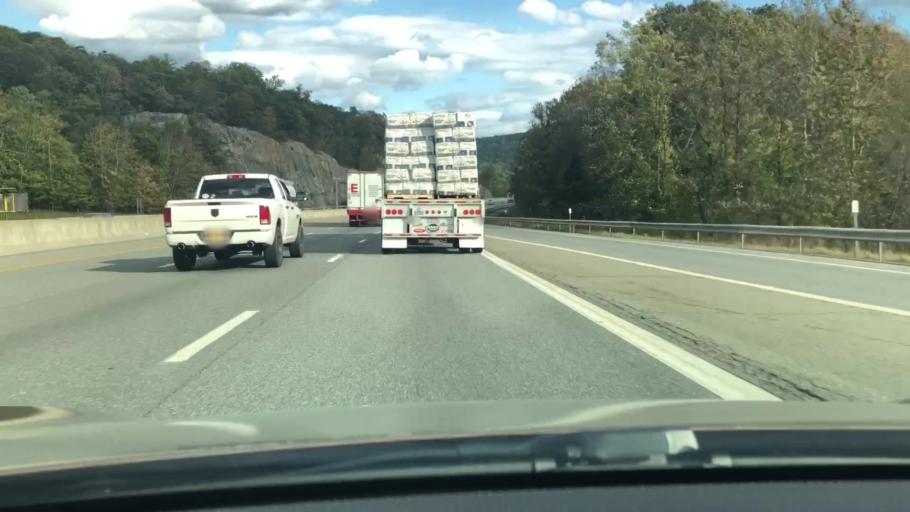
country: US
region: New York
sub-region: Rockland County
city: Sloatsburg
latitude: 41.1426
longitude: -74.1777
